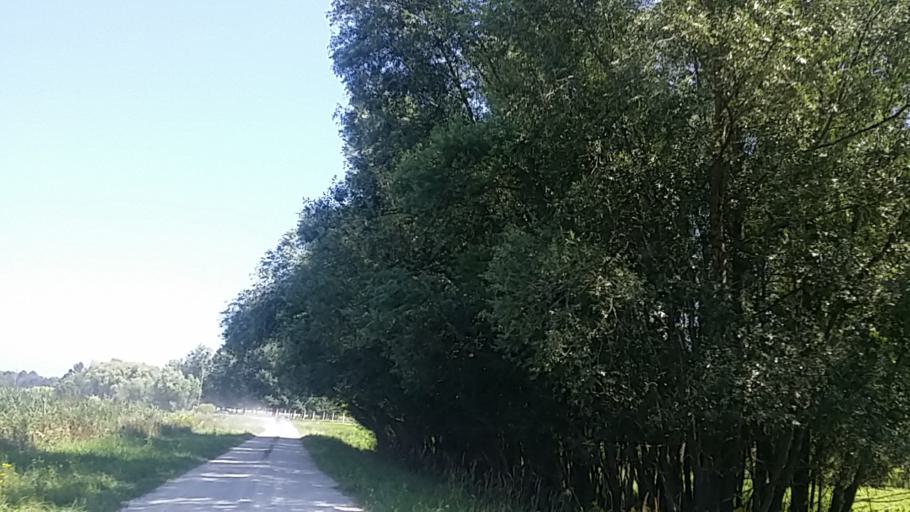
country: HU
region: Zala
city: Sarmellek
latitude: 46.6981
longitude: 17.2367
